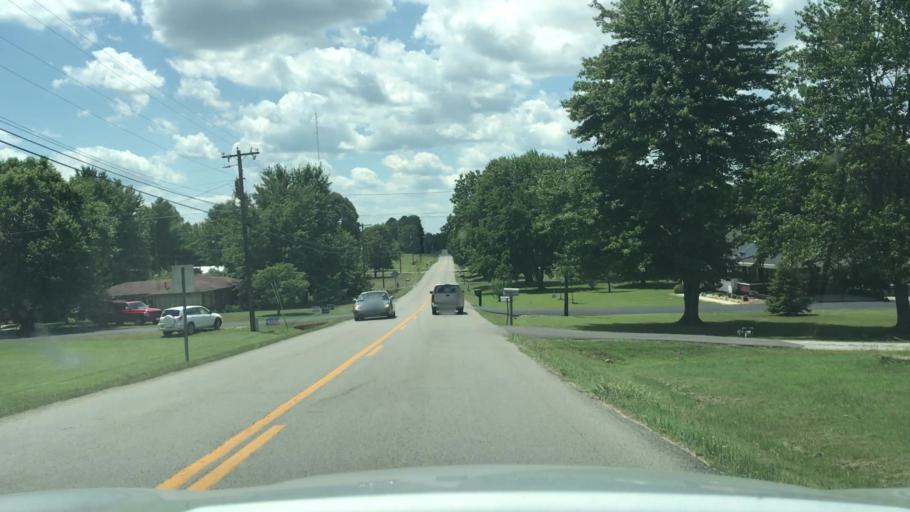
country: US
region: Kentucky
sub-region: Muhlenberg County
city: Greenville
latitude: 37.1982
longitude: -87.2084
